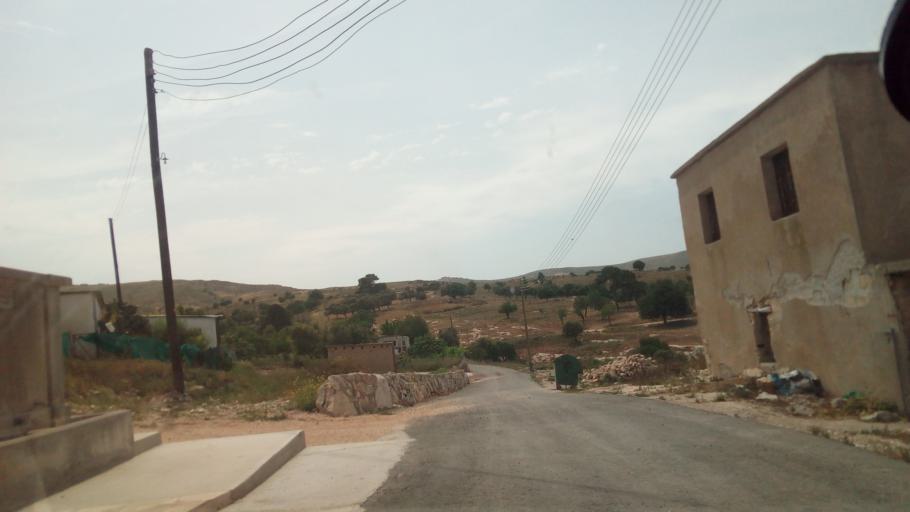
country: CY
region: Pafos
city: Polis
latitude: 34.9996
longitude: 32.3796
